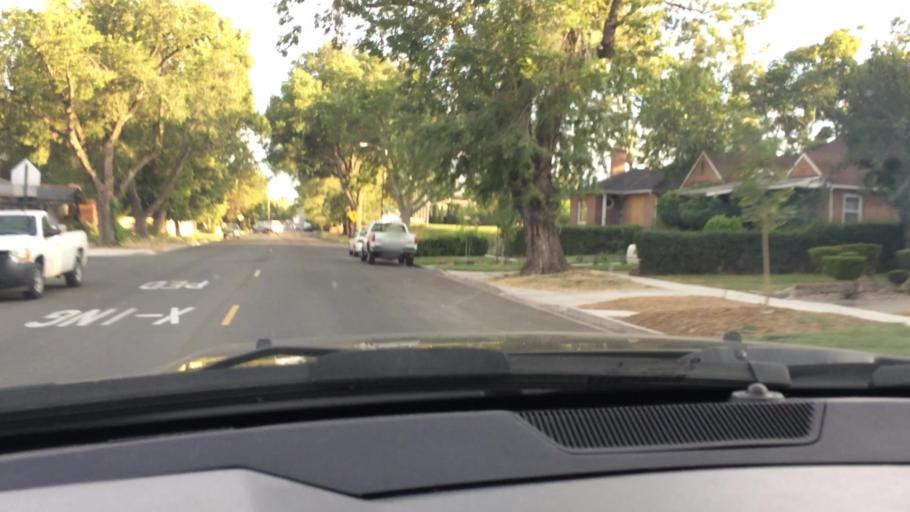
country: US
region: Nevada
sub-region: Washoe County
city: Reno
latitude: 39.5144
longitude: -119.8126
